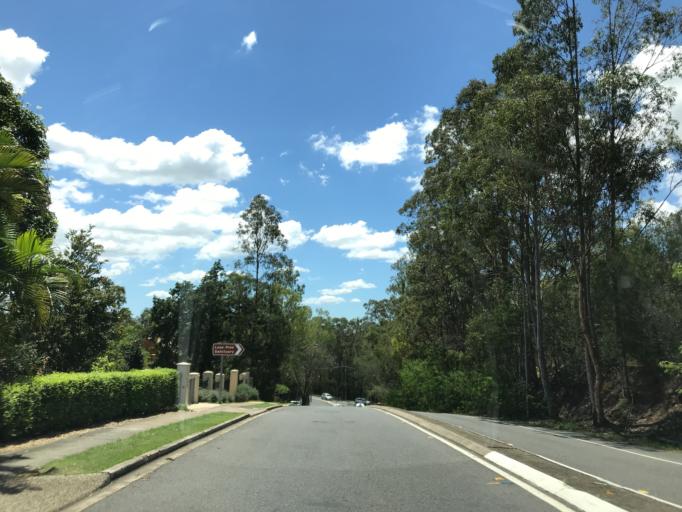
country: AU
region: Queensland
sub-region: Brisbane
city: Seventeen Mile Rocks
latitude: -27.5256
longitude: 152.9547
